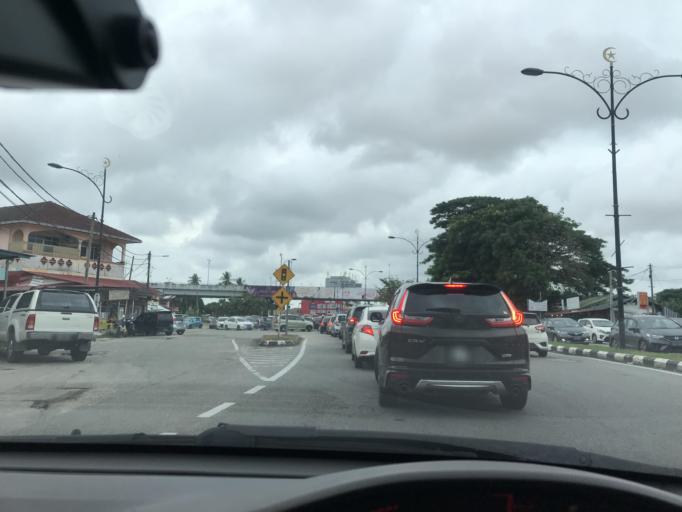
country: MY
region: Kelantan
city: Kota Bharu
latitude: 6.1145
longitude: 102.2372
